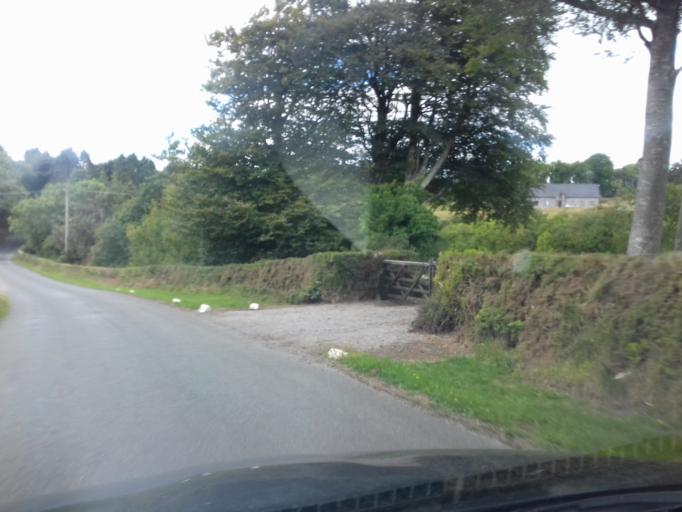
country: IE
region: Munster
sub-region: Waterford
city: Portlaw
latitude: 52.1770
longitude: -7.3633
